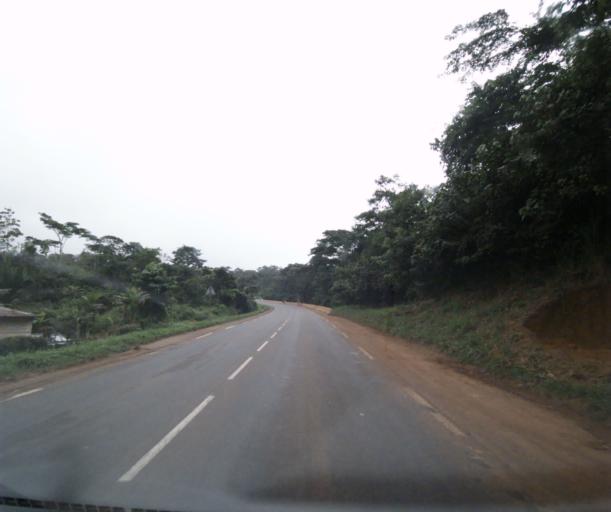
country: CM
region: Centre
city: Mbankomo
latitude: 3.7687
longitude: 11.2099
